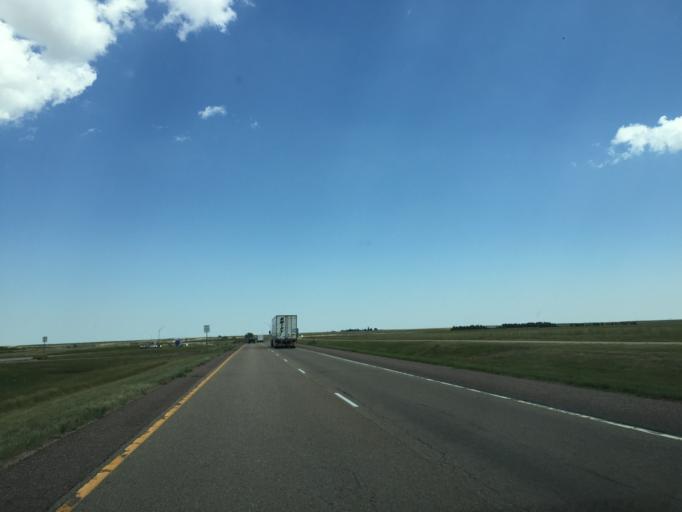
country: US
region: Colorado
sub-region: Lincoln County
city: Hugo
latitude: 39.2788
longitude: -103.4066
